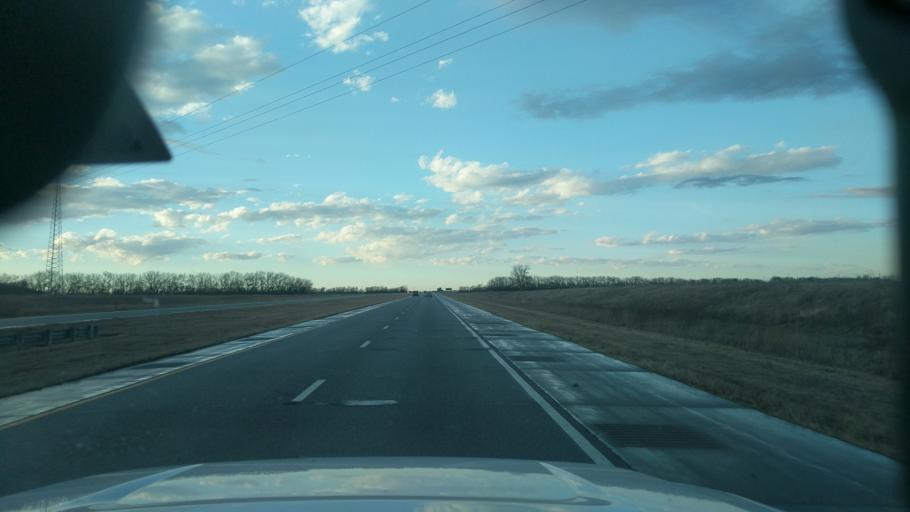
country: US
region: Kansas
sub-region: McPherson County
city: Moundridge
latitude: 38.1885
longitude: -97.4687
